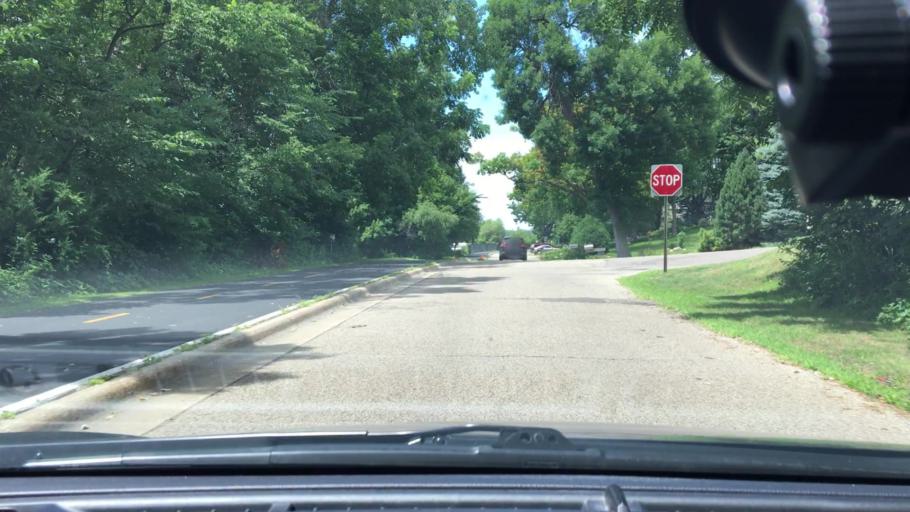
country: US
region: Minnesota
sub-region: Hennepin County
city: New Hope
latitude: 45.0069
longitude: -93.4092
